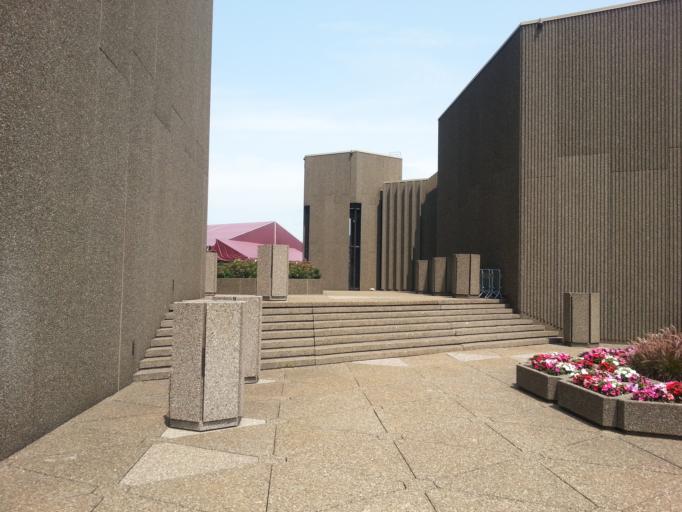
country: CA
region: Ontario
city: Ottawa
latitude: 45.4229
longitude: -75.6935
